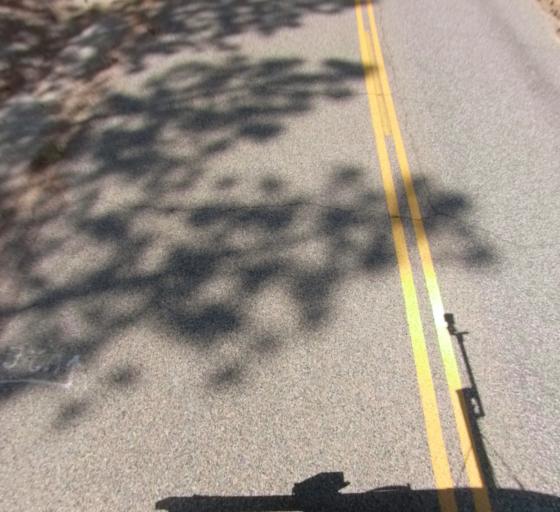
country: US
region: California
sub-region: Madera County
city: Oakhurst
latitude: 37.3974
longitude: -119.3513
